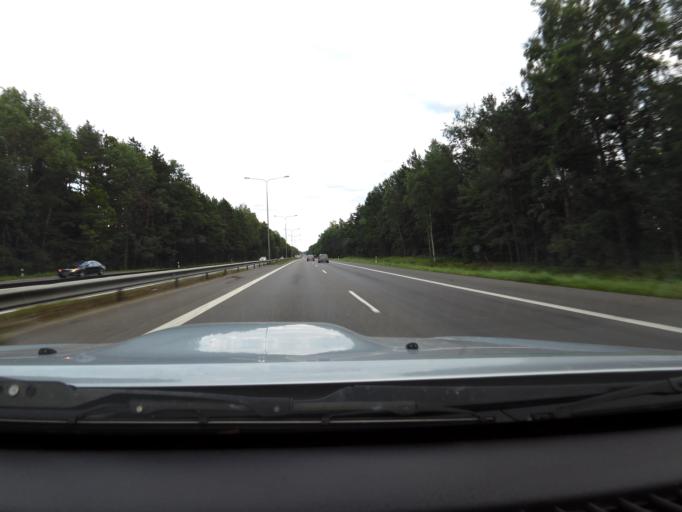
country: LT
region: Kauno apskritis
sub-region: Kauno rajonas
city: Karmelava
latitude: 54.9060
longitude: 24.1194
